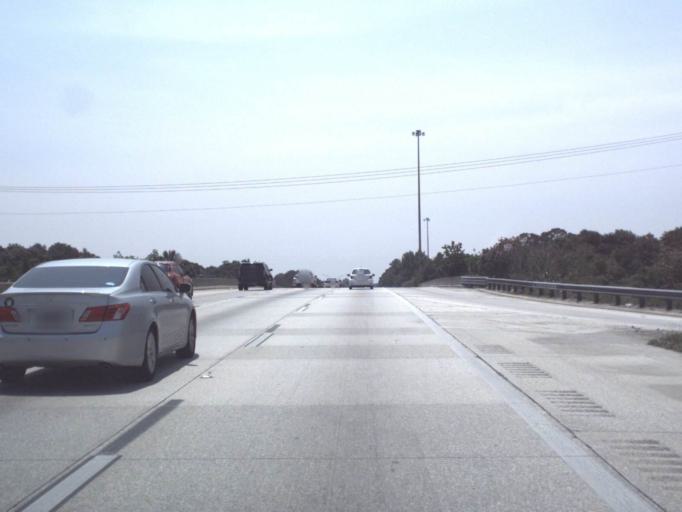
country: US
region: Florida
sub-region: Duval County
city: Jacksonville
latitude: 30.2913
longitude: -81.6306
